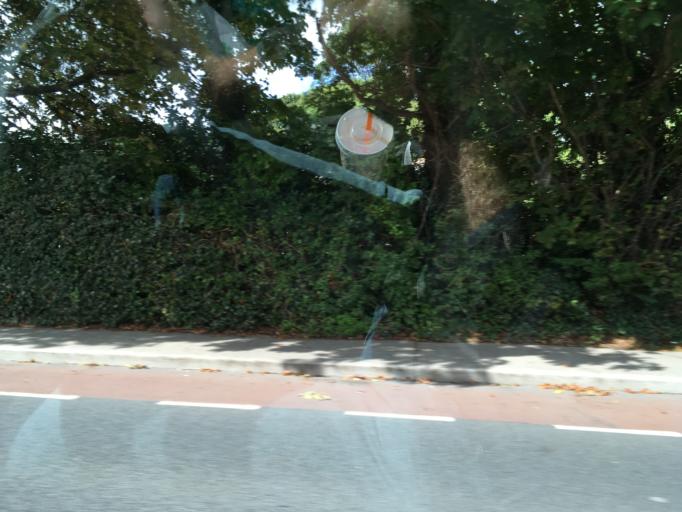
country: IE
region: Leinster
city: Little Bray
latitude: 53.1954
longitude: -6.1179
